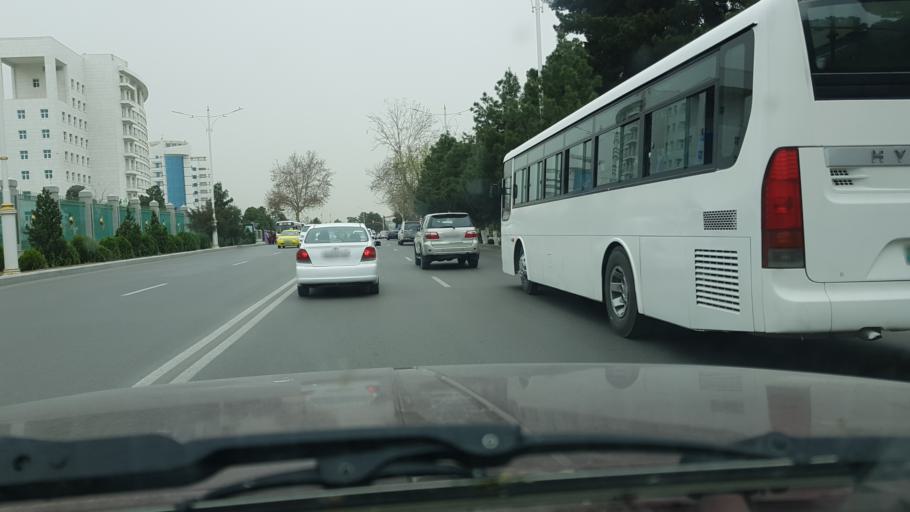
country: TM
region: Ahal
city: Ashgabat
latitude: 37.9509
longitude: 58.3429
